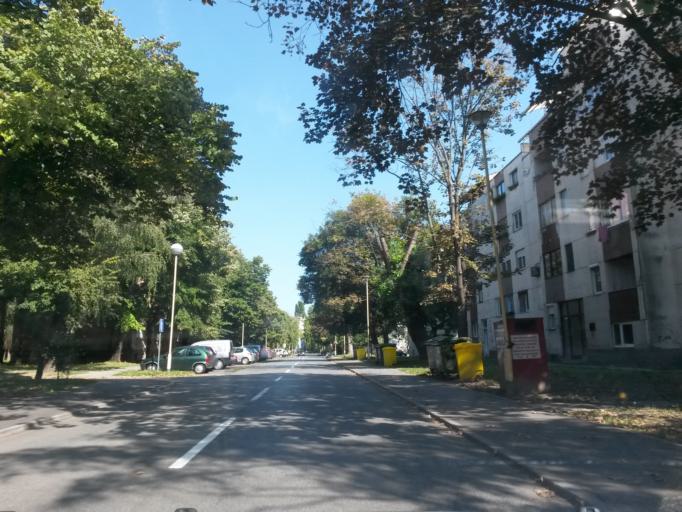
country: HR
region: Osjecko-Baranjska
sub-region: Grad Osijek
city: Osijek
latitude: 45.5571
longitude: 18.6979
